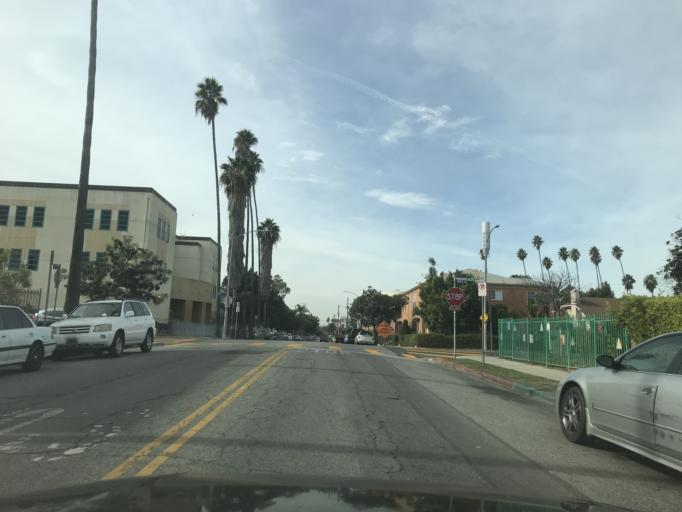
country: US
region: California
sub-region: Los Angeles County
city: Hollywood
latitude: 34.0712
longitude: -118.3038
